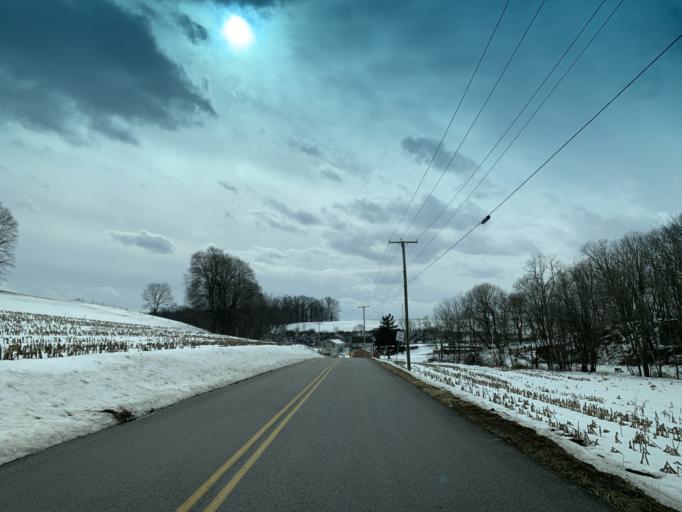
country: US
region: Pennsylvania
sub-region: York County
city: Shrewsbury
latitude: 39.7675
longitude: -76.6501
